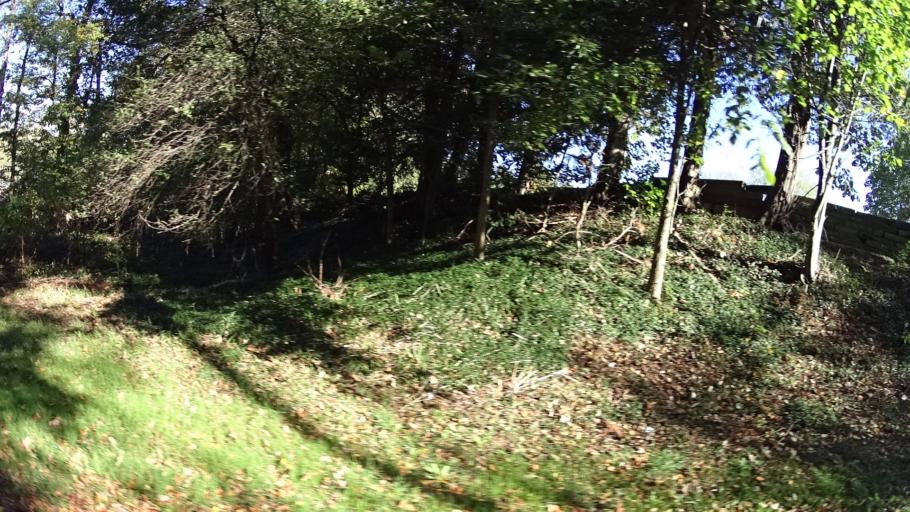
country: US
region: Ohio
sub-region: Lorain County
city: Amherst
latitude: 41.3807
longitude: -82.2391
